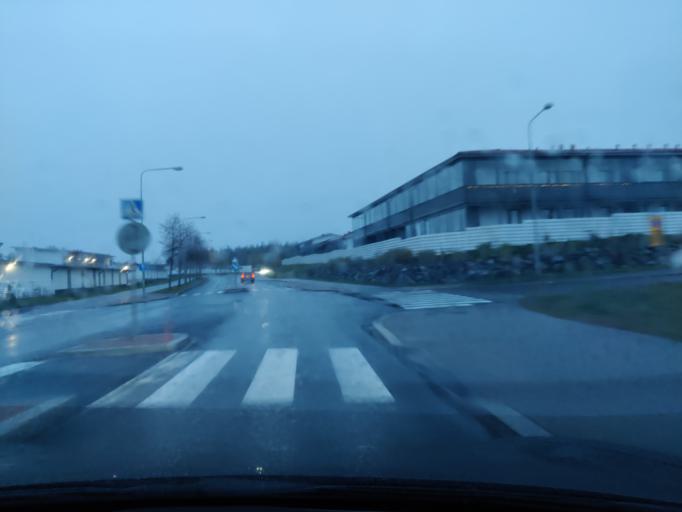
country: FI
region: Northern Savo
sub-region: Kuopio
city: Kuopio
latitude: 62.8281
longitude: 27.6775
